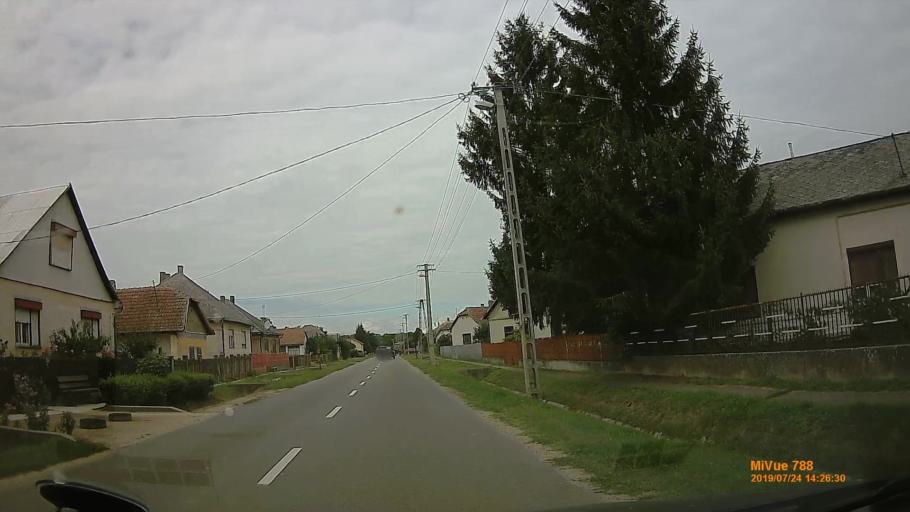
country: HU
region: Szabolcs-Szatmar-Bereg
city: Mandok
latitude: 48.3271
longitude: 22.2653
